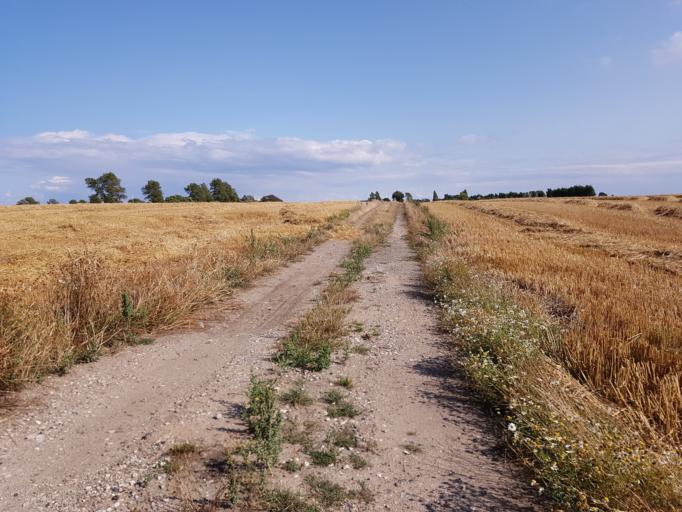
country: DK
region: Zealand
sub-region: Guldborgsund Kommune
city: Nykobing Falster
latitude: 54.5892
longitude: 11.9358
